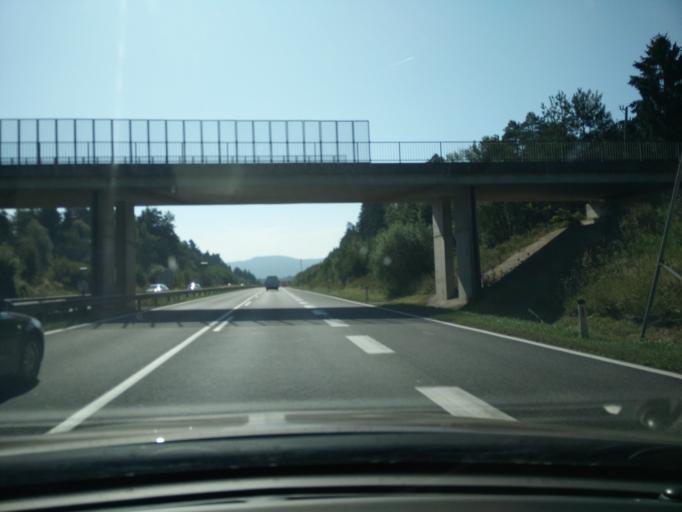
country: SI
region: Vodice
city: Vodice
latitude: 46.1932
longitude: 14.4745
